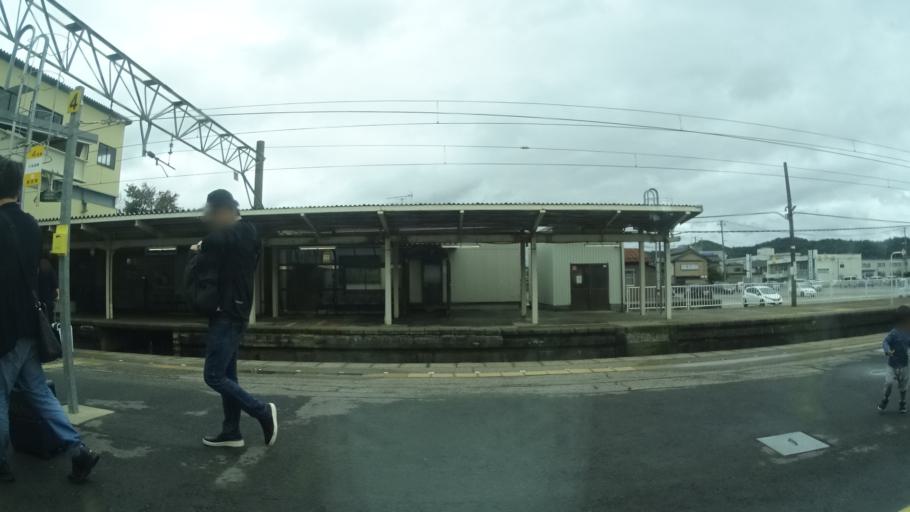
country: JP
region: Niigata
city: Murakami
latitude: 38.2199
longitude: 139.4633
